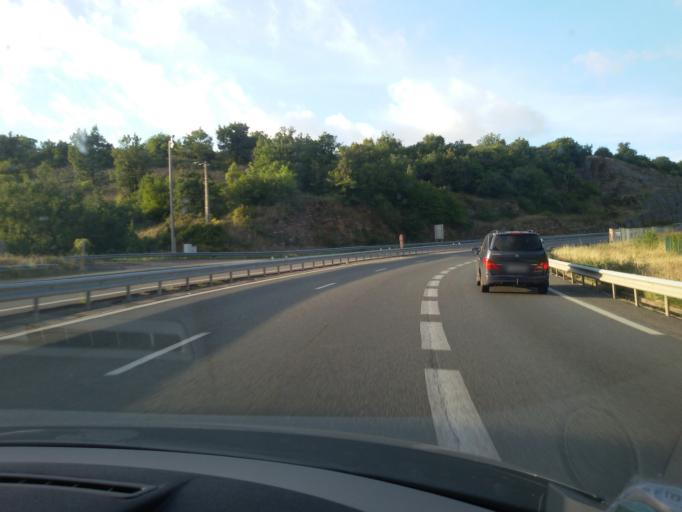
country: FR
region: Languedoc-Roussillon
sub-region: Departement de l'Herault
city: Lodeve
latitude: 43.8353
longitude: 3.3079
